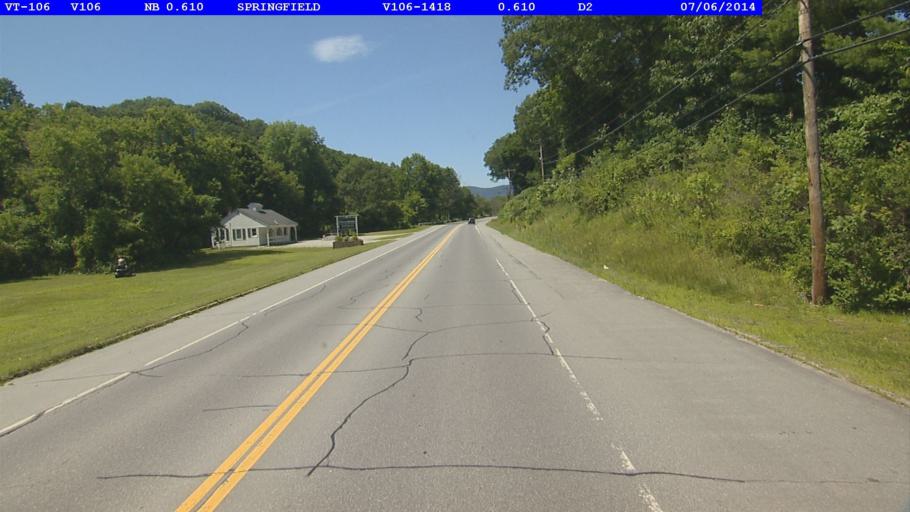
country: US
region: Vermont
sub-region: Windsor County
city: Springfield
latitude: 43.3109
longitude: -72.4988
